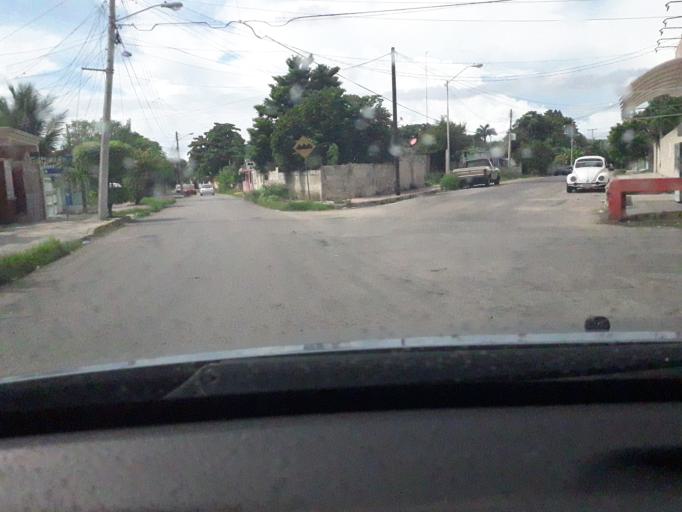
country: MX
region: Yucatan
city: Merida
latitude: 20.9655
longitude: -89.6584
